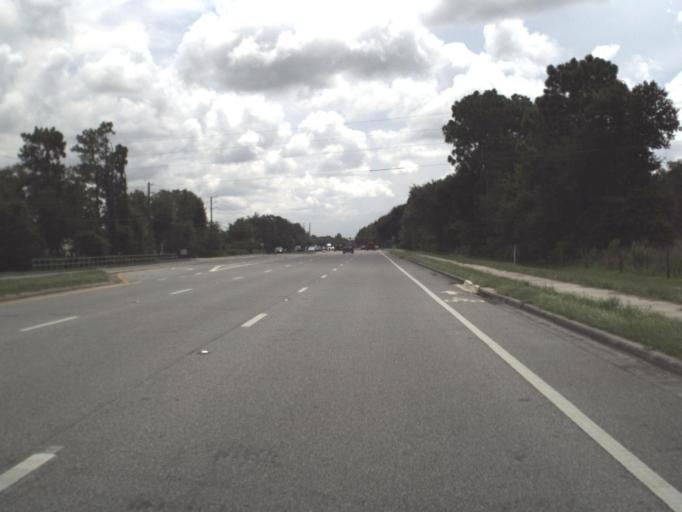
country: US
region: Florida
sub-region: Pasco County
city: Shady Hills
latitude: 28.3291
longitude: -82.5748
